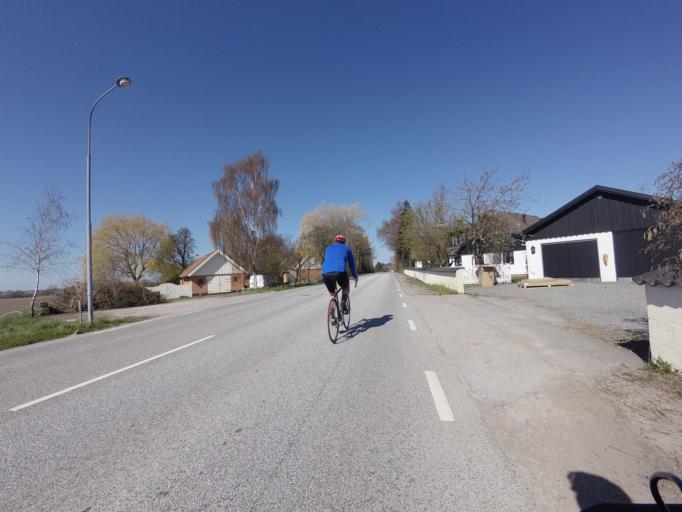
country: SE
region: Skane
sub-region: Vellinge Kommun
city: Vellinge
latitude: 55.4682
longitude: 13.0532
